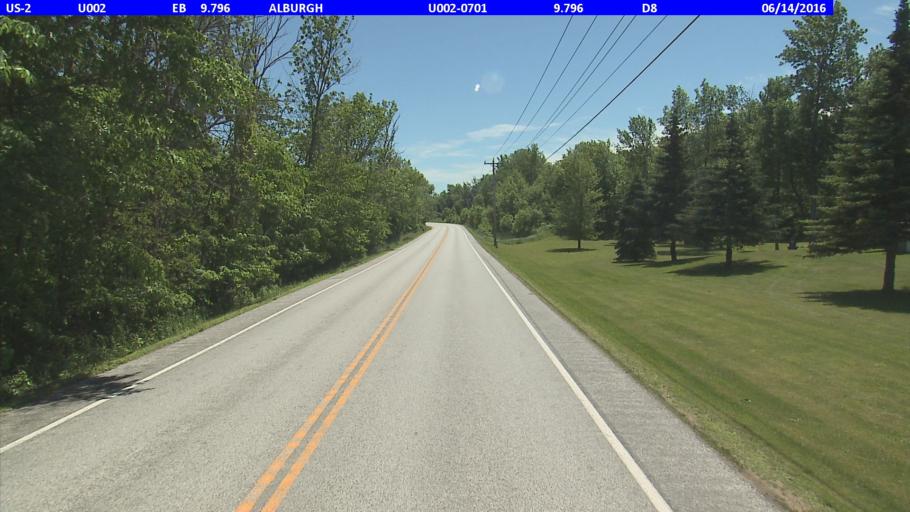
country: US
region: Vermont
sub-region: Grand Isle County
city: North Hero
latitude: 44.9099
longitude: -73.2800
